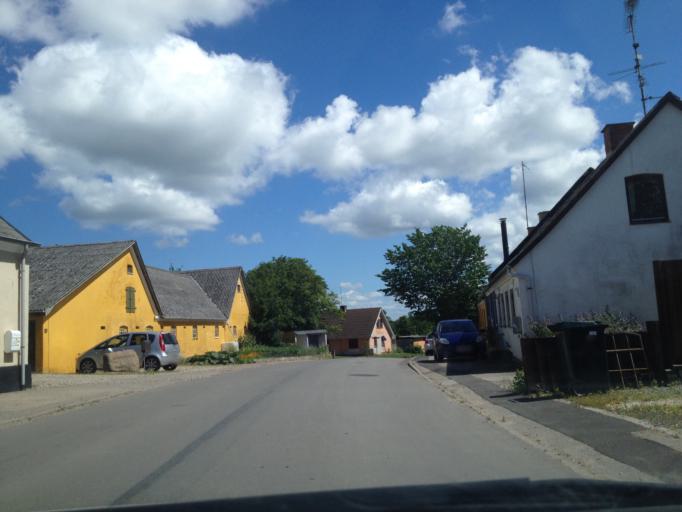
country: DK
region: Zealand
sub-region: Odsherred Kommune
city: Hojby
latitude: 55.9131
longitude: 11.5648
